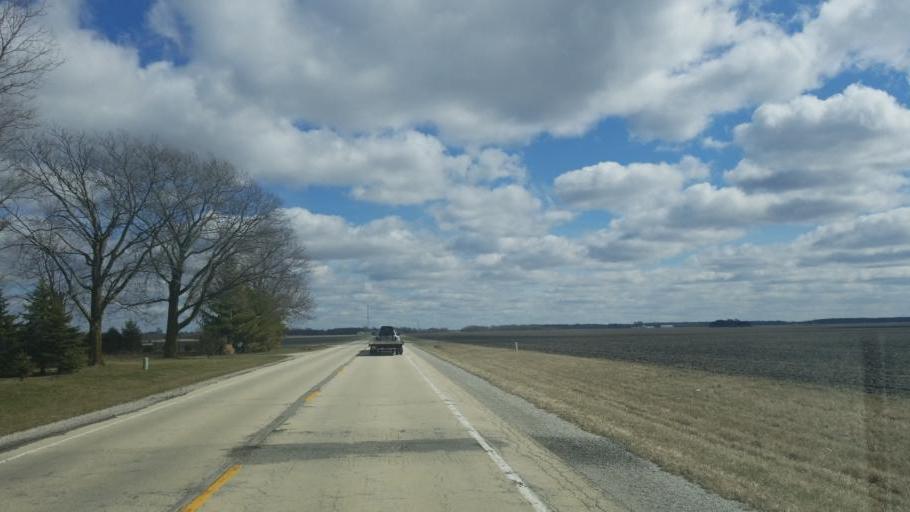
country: US
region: Illinois
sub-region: Douglas County
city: Atwood
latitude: 39.7920
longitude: -88.4907
